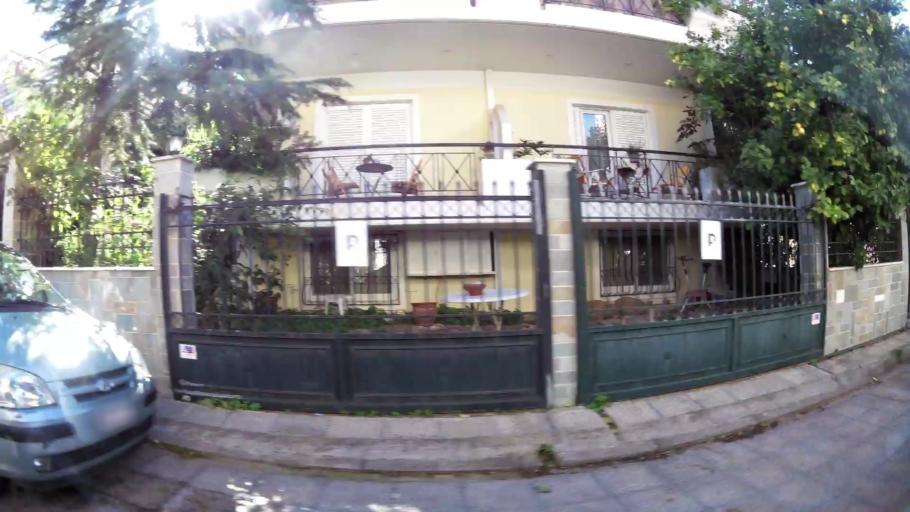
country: GR
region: Attica
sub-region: Nomarchia Athinas
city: Agia Paraskevi
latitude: 38.0062
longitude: 23.8479
